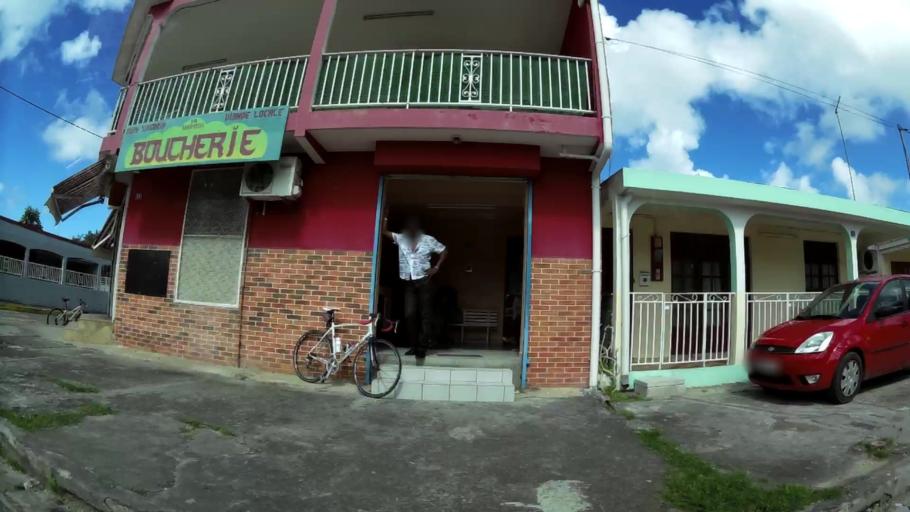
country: GP
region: Guadeloupe
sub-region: Guadeloupe
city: Port-Louis
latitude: 16.4186
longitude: -61.5307
